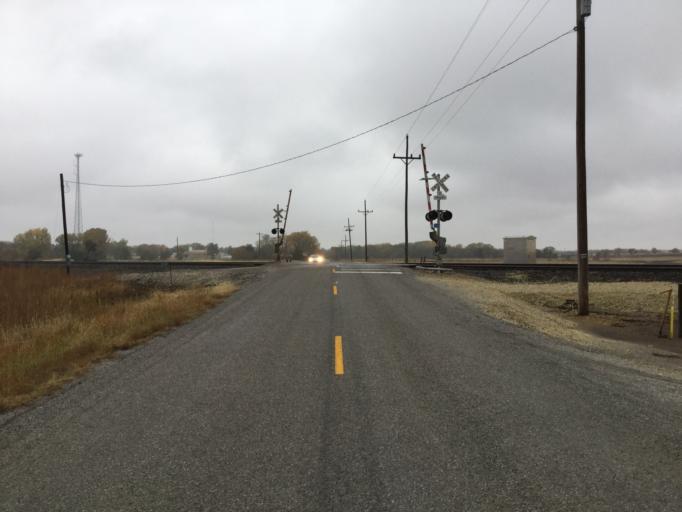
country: US
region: Kansas
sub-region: Butler County
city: El Dorado
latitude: 38.0428
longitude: -96.6319
